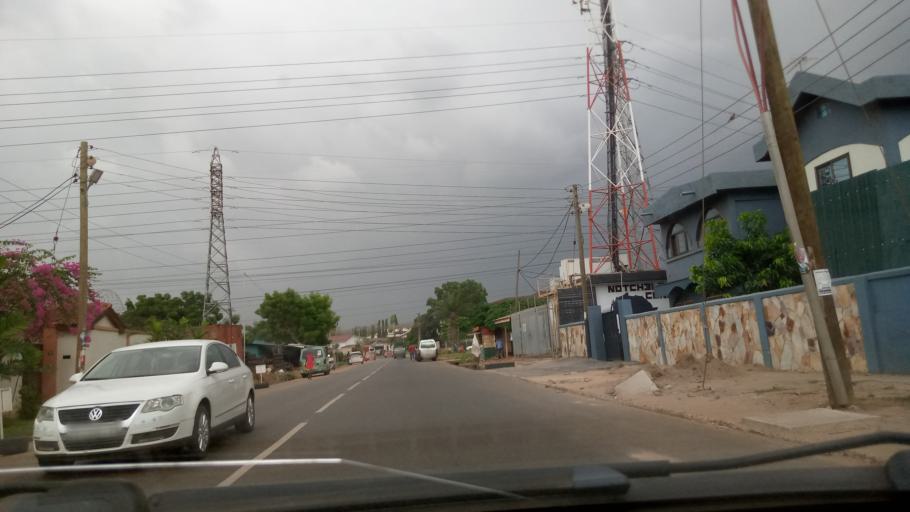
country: GH
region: Greater Accra
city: Dome
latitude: 5.6148
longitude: -0.1961
